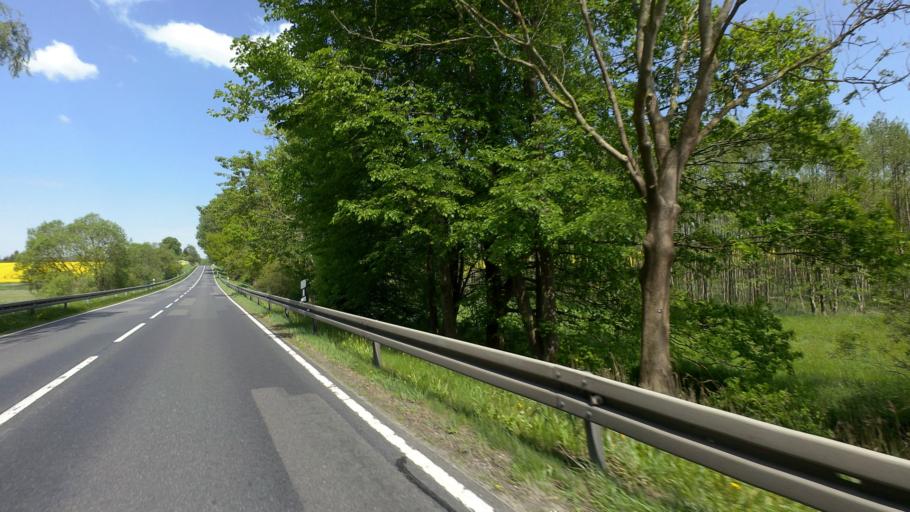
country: DE
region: Mecklenburg-Vorpommern
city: Mollenhagen
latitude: 53.5657
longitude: 12.8623
